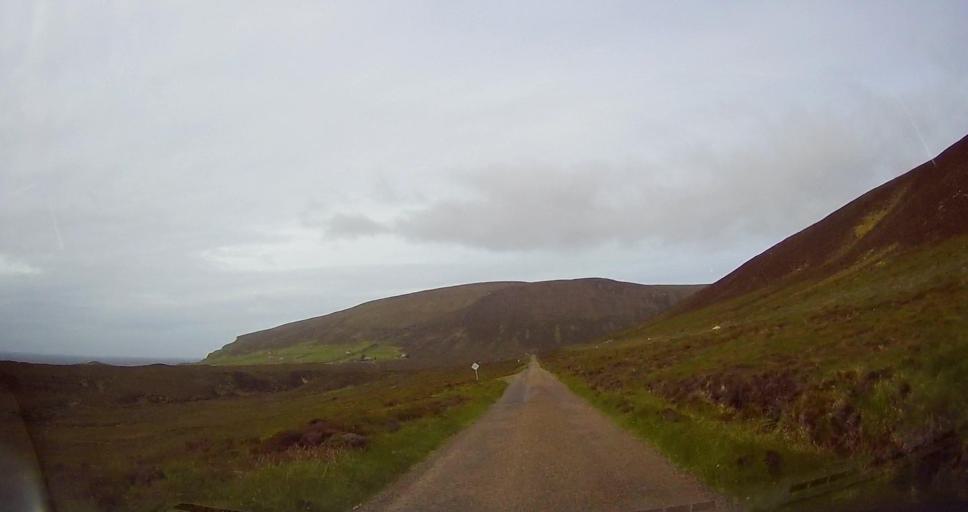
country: GB
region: Scotland
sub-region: Orkney Islands
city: Stromness
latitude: 58.8816
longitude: -3.3645
